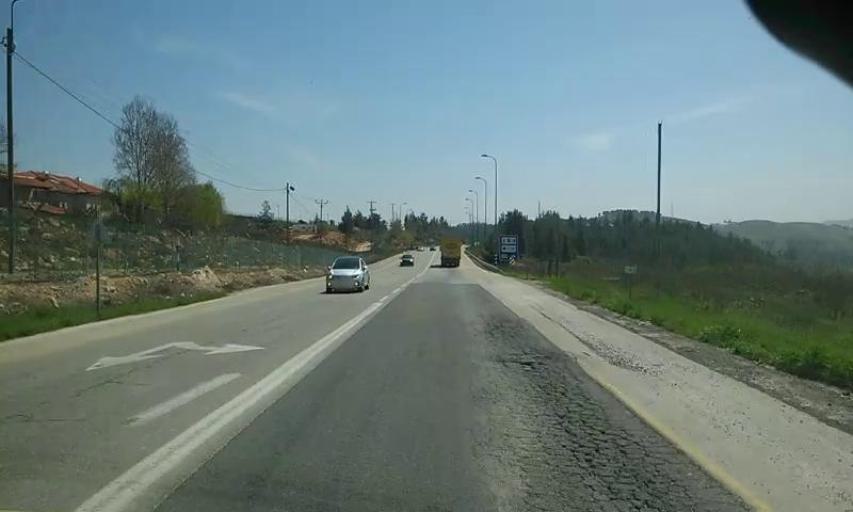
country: PS
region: West Bank
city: Bayt Ummar
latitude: 31.6502
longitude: 35.1267
